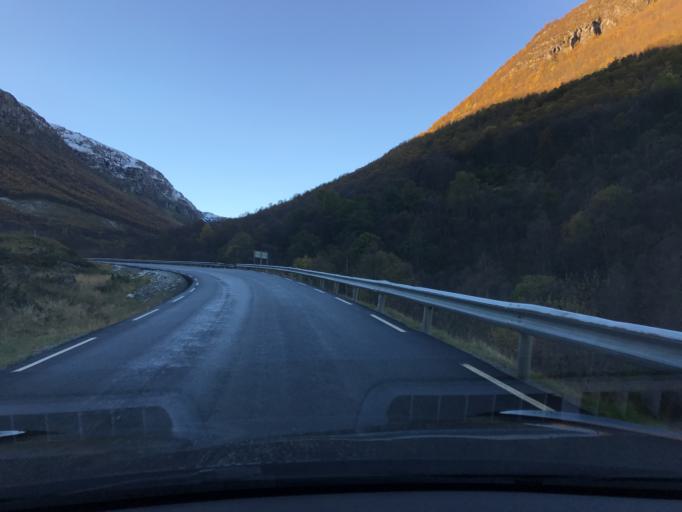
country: NO
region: Sogn og Fjordane
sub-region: Aurland
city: Aurlandsvangen
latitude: 60.8498
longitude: 7.3106
